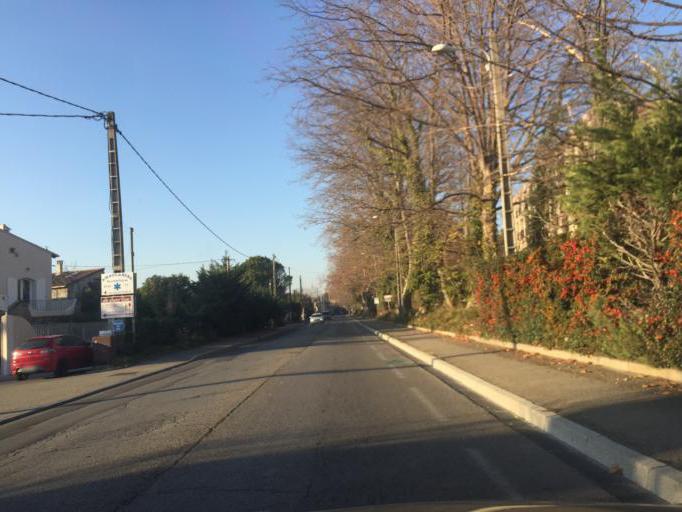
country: FR
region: Provence-Alpes-Cote d'Azur
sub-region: Departement du Vaucluse
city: Montfavet
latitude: 43.9300
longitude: 4.8749
